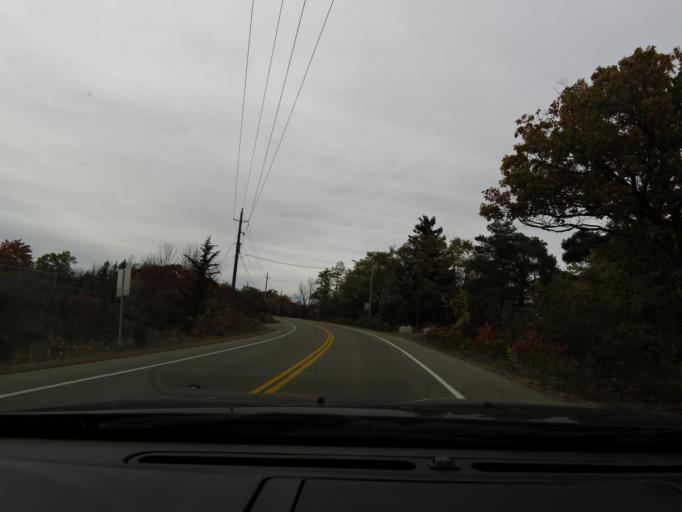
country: CA
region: Ontario
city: Hamilton
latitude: 43.2979
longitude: -79.8842
